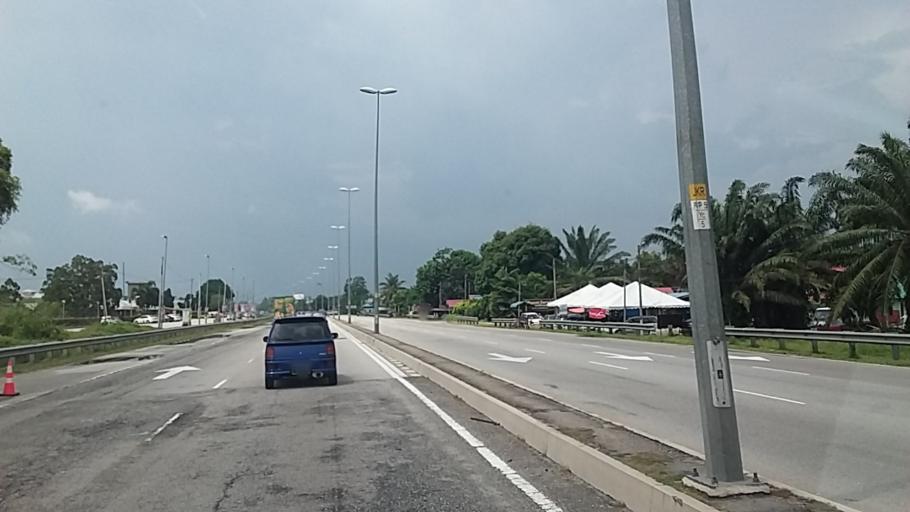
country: MY
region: Johor
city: Parit Raja
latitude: 1.8539
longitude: 103.0912
